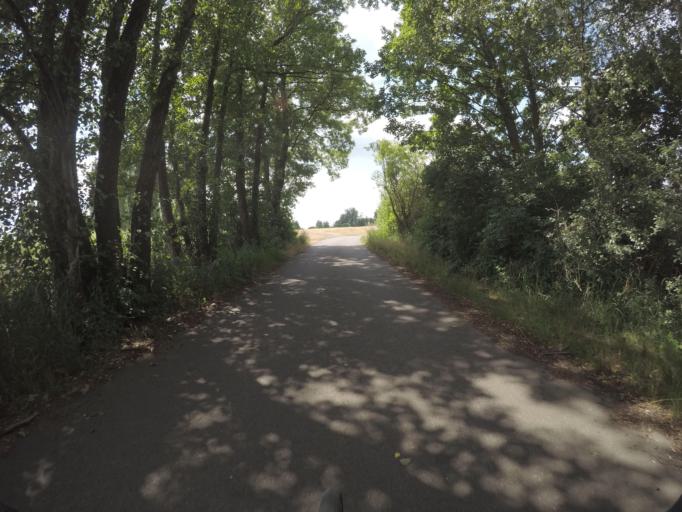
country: DE
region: Brandenburg
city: Roskow
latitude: 52.4496
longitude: 12.6776
